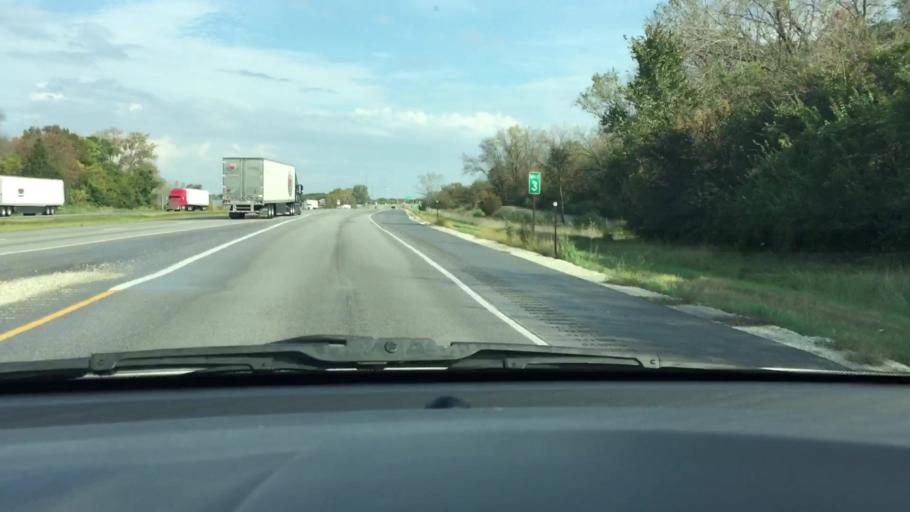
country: US
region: Iowa
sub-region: Scott County
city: Le Claire
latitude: 41.5425
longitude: -90.3413
